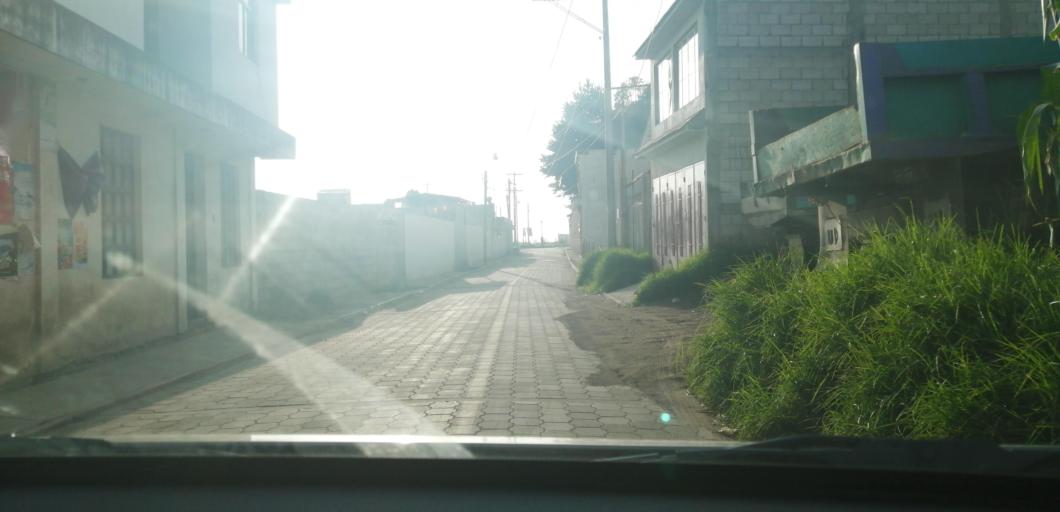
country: GT
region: Quetzaltenango
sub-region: Municipio de La Esperanza
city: La Esperanza
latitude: 14.8685
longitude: -91.5484
